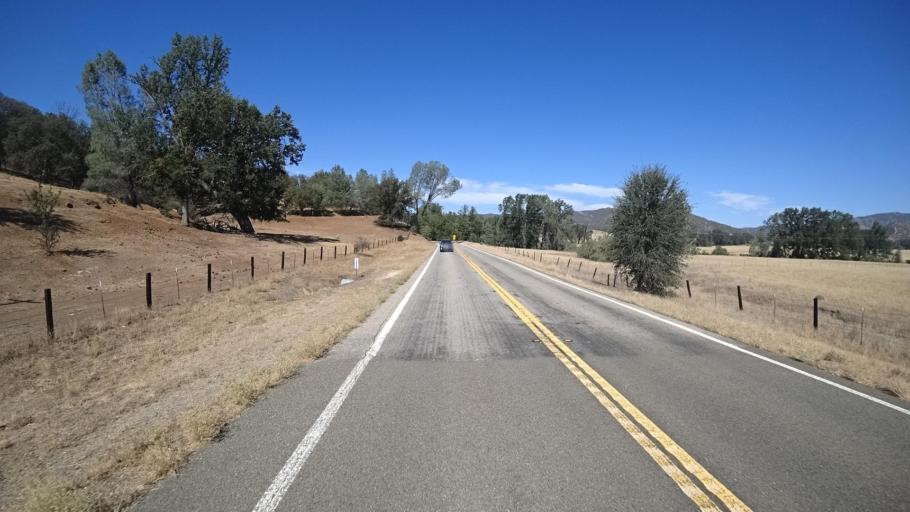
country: US
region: California
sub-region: Fresno County
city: Coalinga
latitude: 36.1946
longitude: -120.7102
